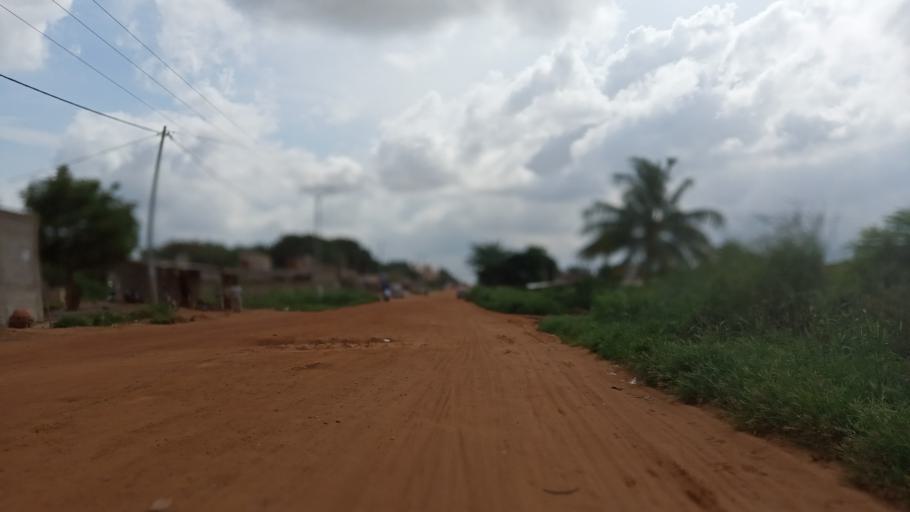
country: TG
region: Maritime
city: Lome
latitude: 6.2334
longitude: 1.1419
